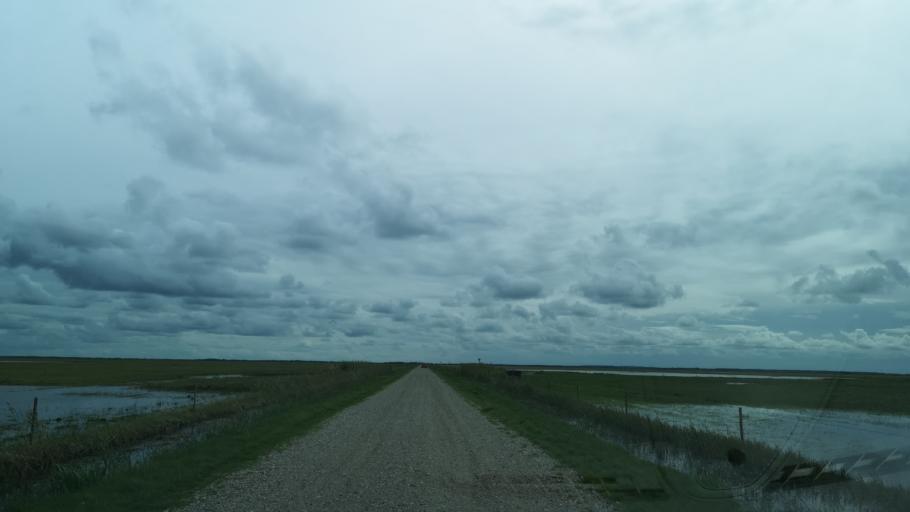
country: DK
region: Central Jutland
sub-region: Ringkobing-Skjern Kommune
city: Hvide Sande
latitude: 55.8892
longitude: 8.2173
